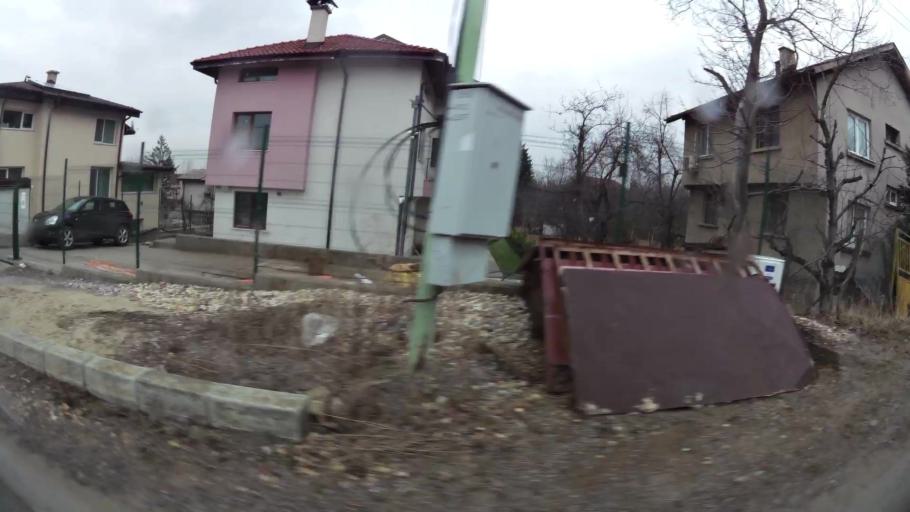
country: BG
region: Sofia-Capital
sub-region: Stolichna Obshtina
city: Sofia
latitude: 42.6180
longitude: 23.3704
